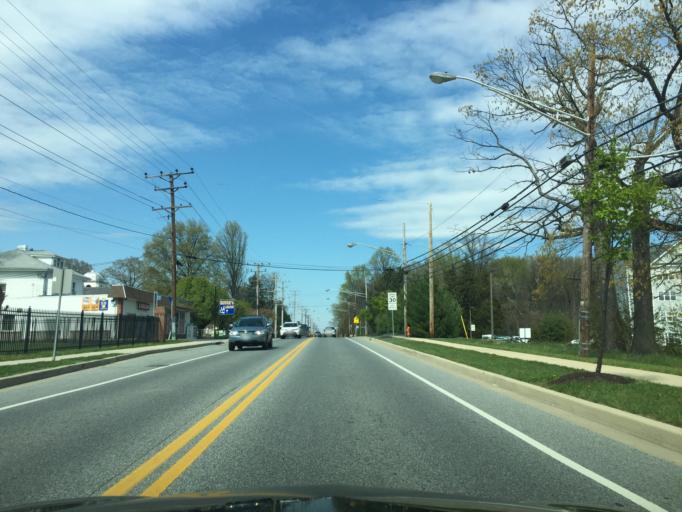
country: US
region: Maryland
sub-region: Baltimore County
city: Middle River
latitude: 39.3189
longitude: -76.4484
